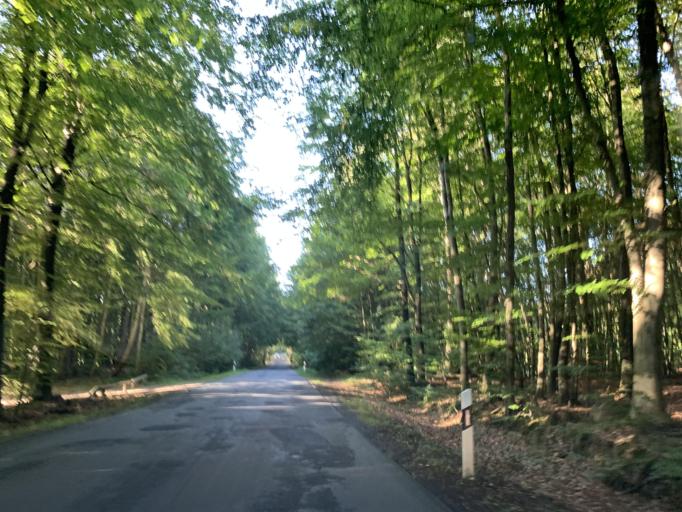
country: DE
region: Mecklenburg-Vorpommern
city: Carpin
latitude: 53.3334
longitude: 13.2431
